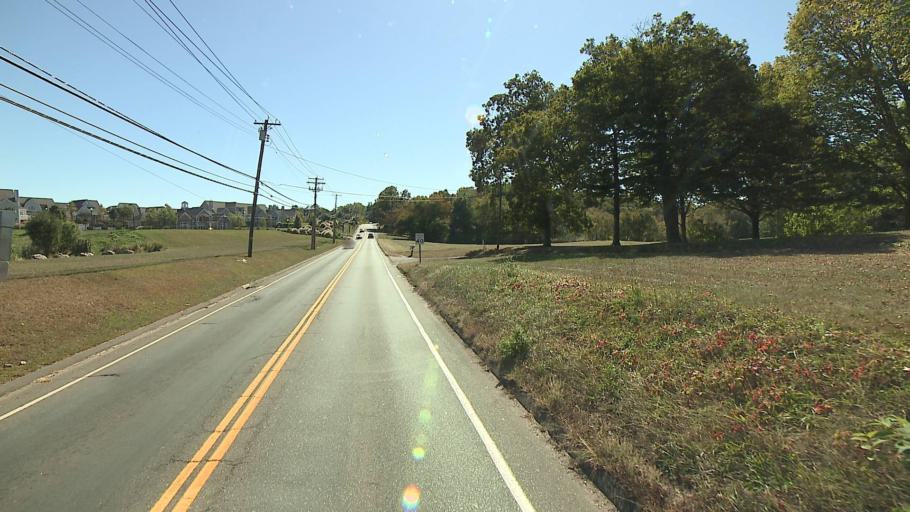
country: US
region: Connecticut
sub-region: New Haven County
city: Orange
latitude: 41.3103
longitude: -73.0466
